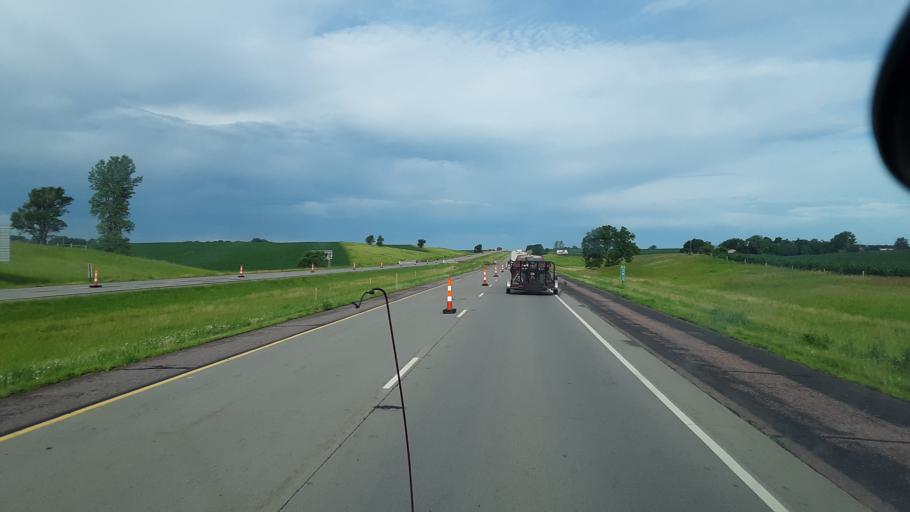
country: US
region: South Dakota
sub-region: Minnehaha County
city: Crooks
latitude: 43.6087
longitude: -96.8390
